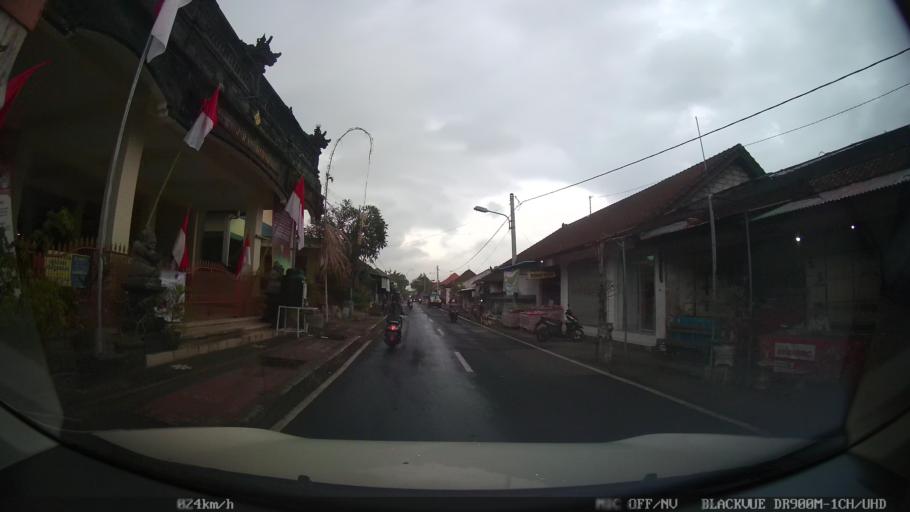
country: ID
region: Bali
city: Banjar Pasekan
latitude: -8.5977
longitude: 115.2828
